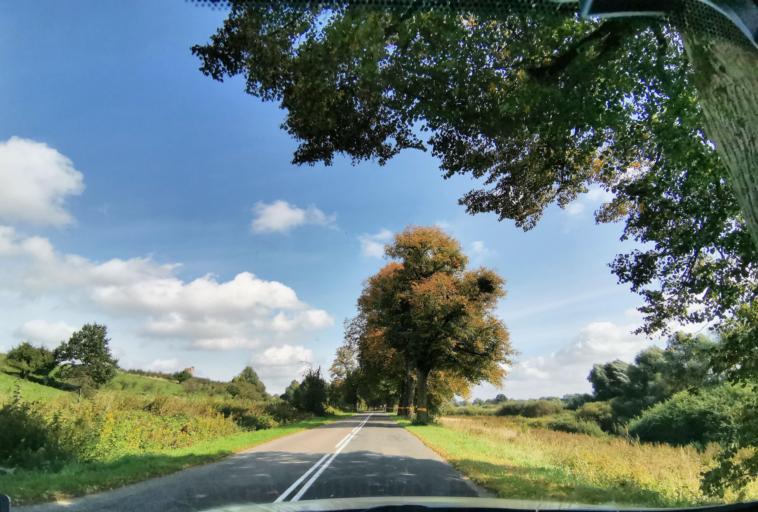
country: RU
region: Kaliningrad
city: Chernyakhovsk
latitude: 54.6506
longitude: 21.7836
